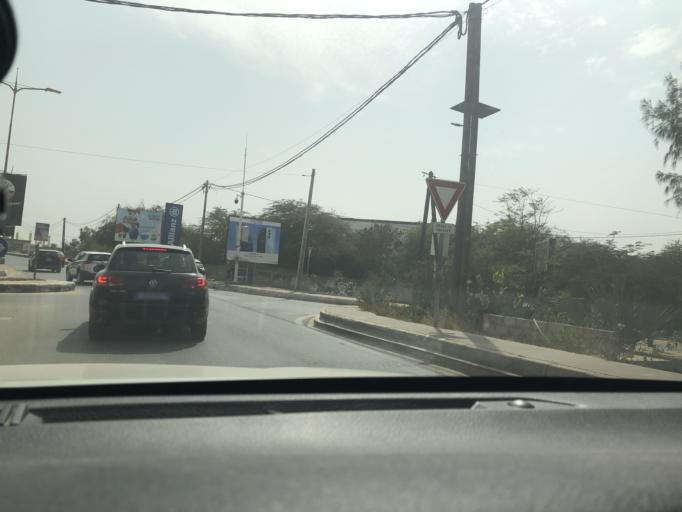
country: SN
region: Dakar
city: Mermoz Boabab
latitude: 14.7330
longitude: -17.5084
